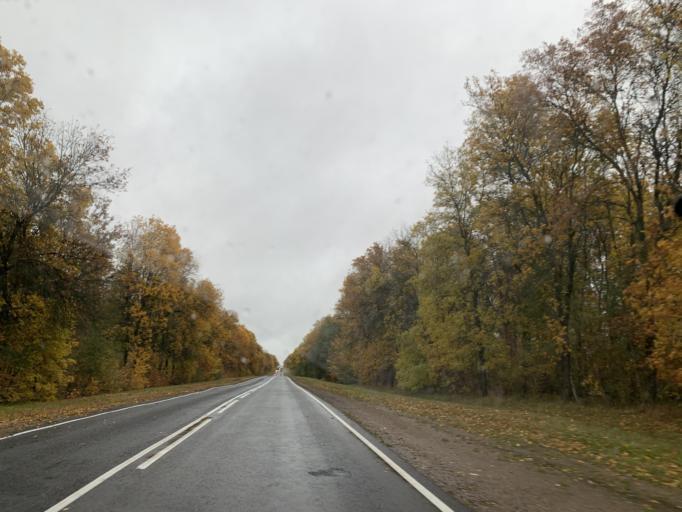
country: BY
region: Minsk
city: Novy Svyerzhan'
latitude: 53.4390
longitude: 26.6552
